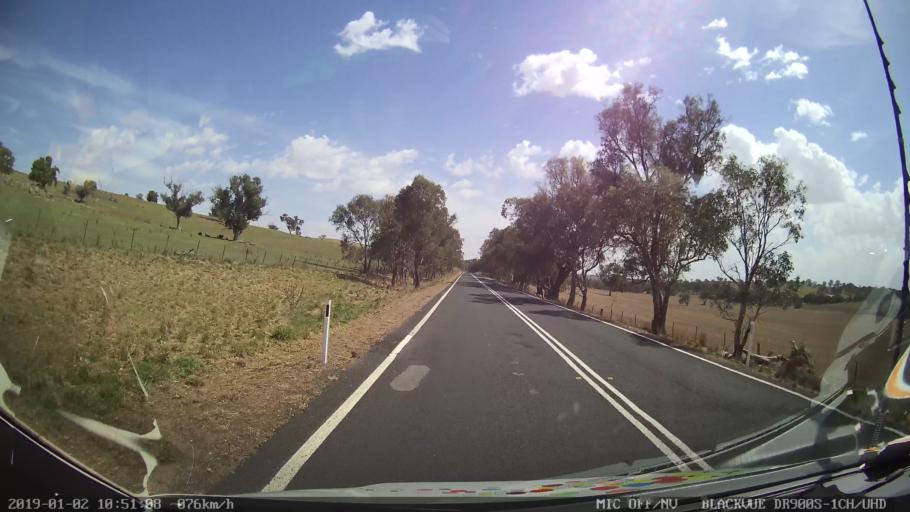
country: AU
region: New South Wales
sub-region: Cootamundra
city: Cootamundra
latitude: -34.7042
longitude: 148.2756
